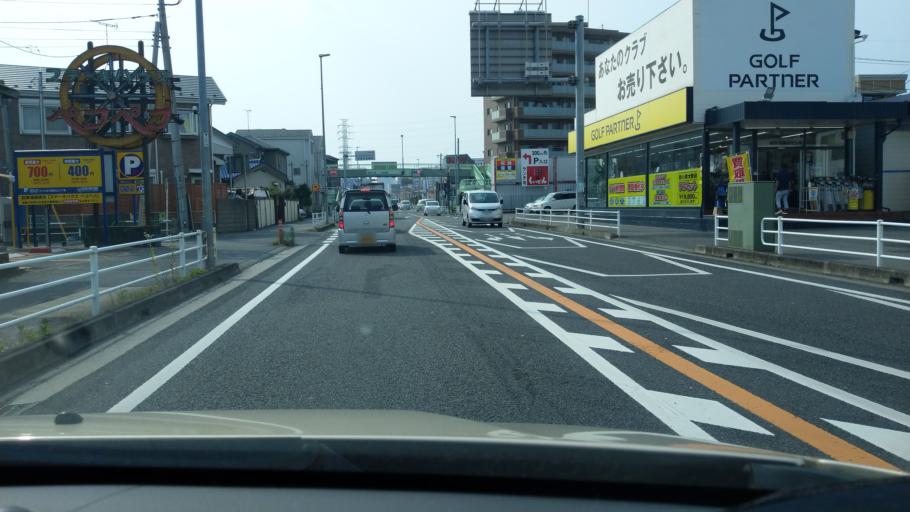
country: JP
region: Saitama
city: Shimotoda
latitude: 35.8364
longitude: 139.6649
